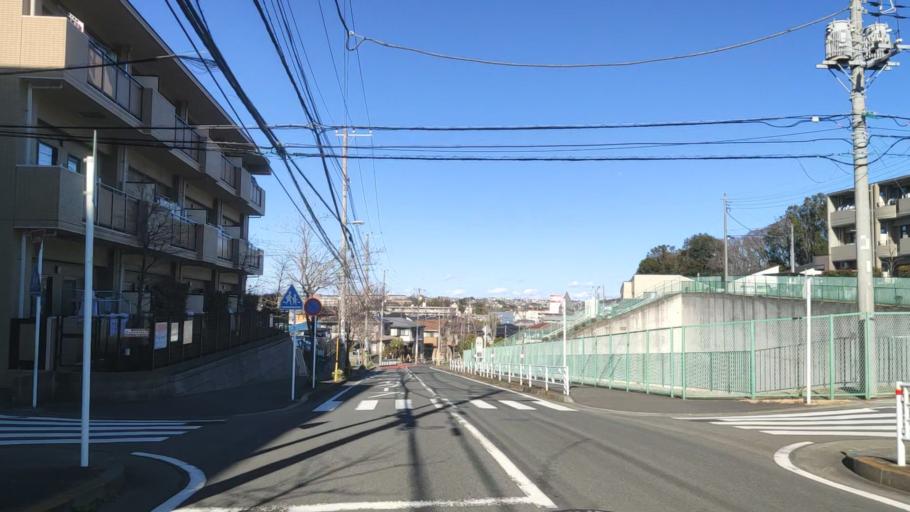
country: JP
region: Kanagawa
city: Minami-rinkan
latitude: 35.5098
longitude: 139.5350
